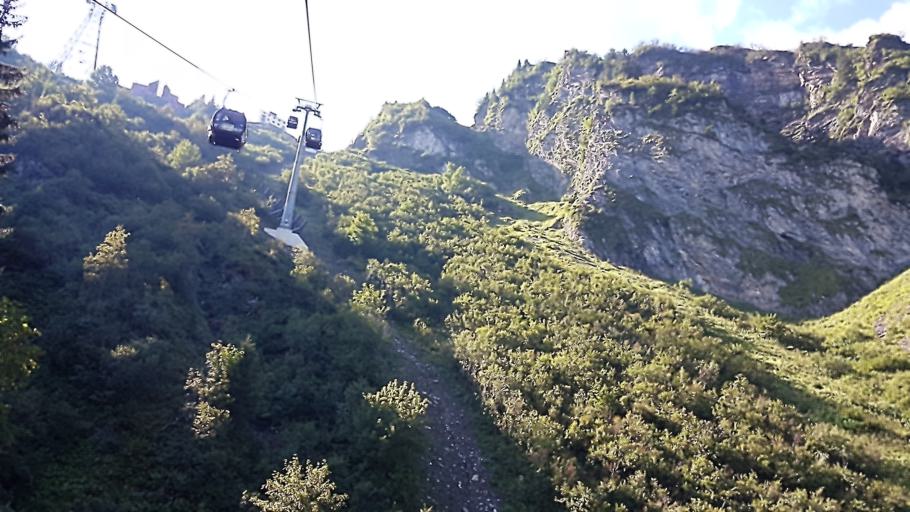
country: CH
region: Obwalden
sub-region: Obwalden
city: Engelberg
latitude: 46.7970
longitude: 8.3977
